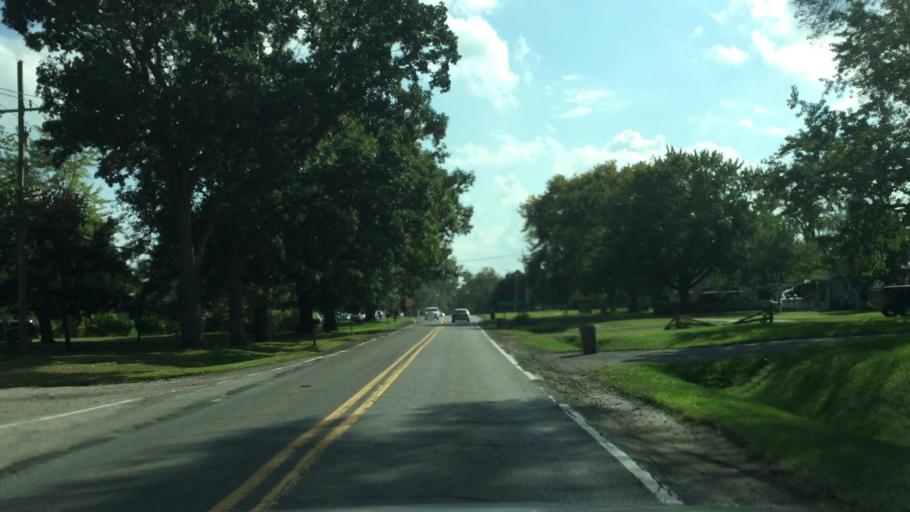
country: US
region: Michigan
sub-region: Oakland County
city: Waterford
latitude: 42.6554
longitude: -83.3862
